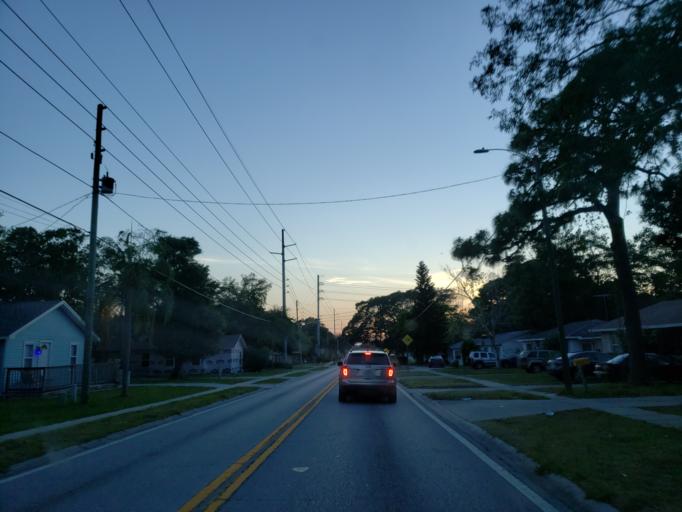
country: US
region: Florida
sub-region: Pinellas County
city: Largo
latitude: 27.9094
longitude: -82.7980
